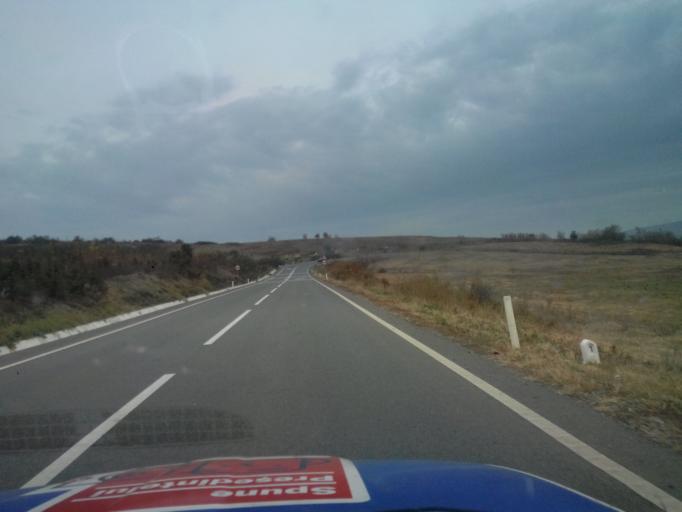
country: RO
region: Vaslui
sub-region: Comuna Tatarani
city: Tatarani
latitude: 46.6339
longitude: 27.9539
